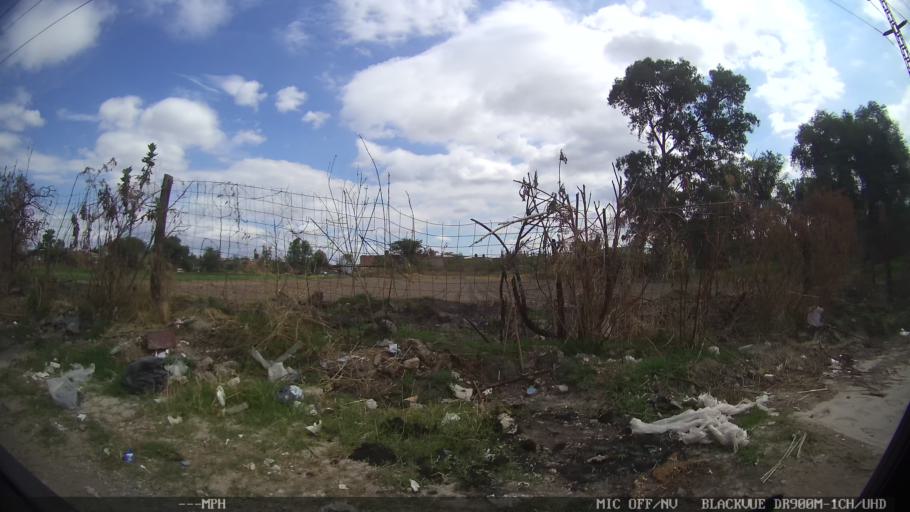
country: MX
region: Jalisco
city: Tonala
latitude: 20.6661
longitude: -103.2501
